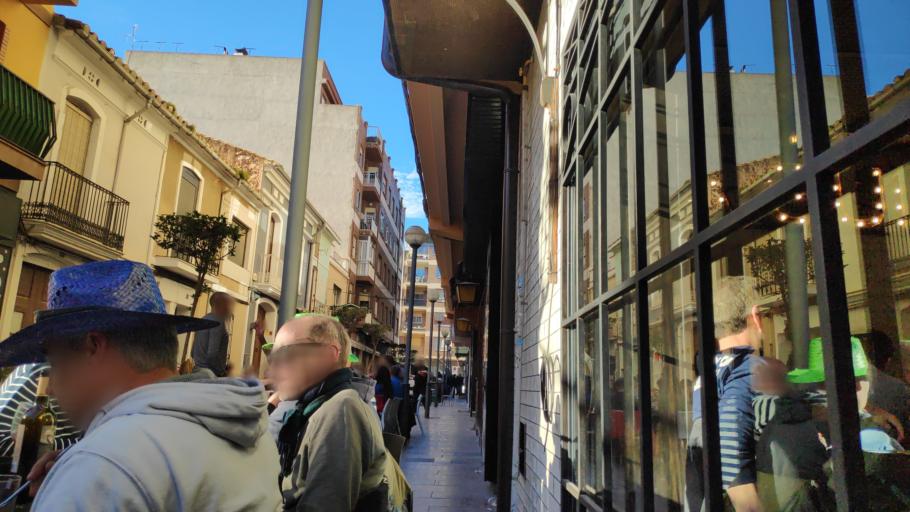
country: ES
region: Valencia
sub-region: Provincia de Castello
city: Benicassim
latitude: 40.0543
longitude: 0.0639
